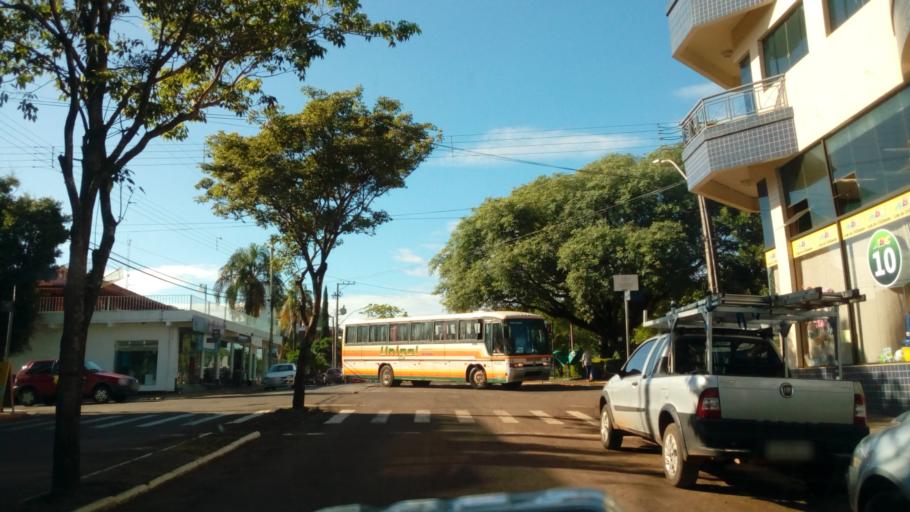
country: AR
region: Misiones
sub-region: Departamento de San Javier
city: San Javier
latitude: -27.9052
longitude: -55.1388
